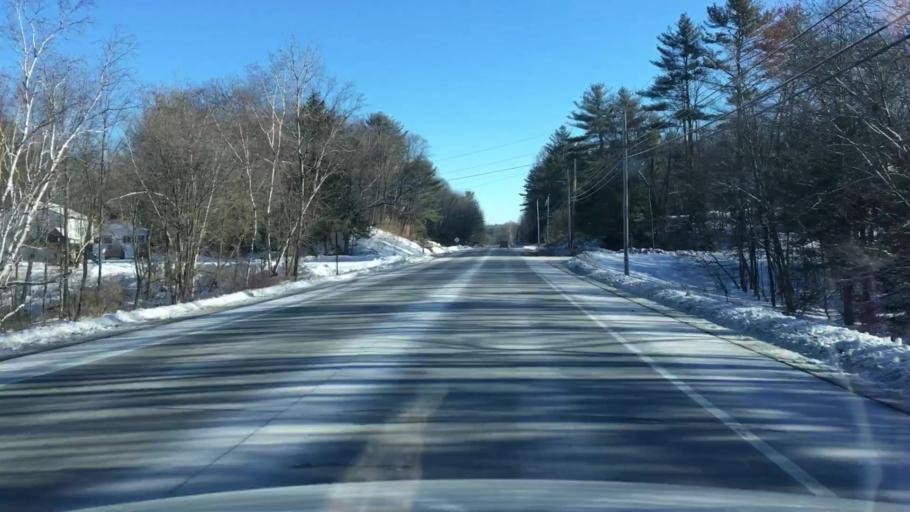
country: US
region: Maine
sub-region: Kennebec County
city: Readfield
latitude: 44.3908
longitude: -69.9822
